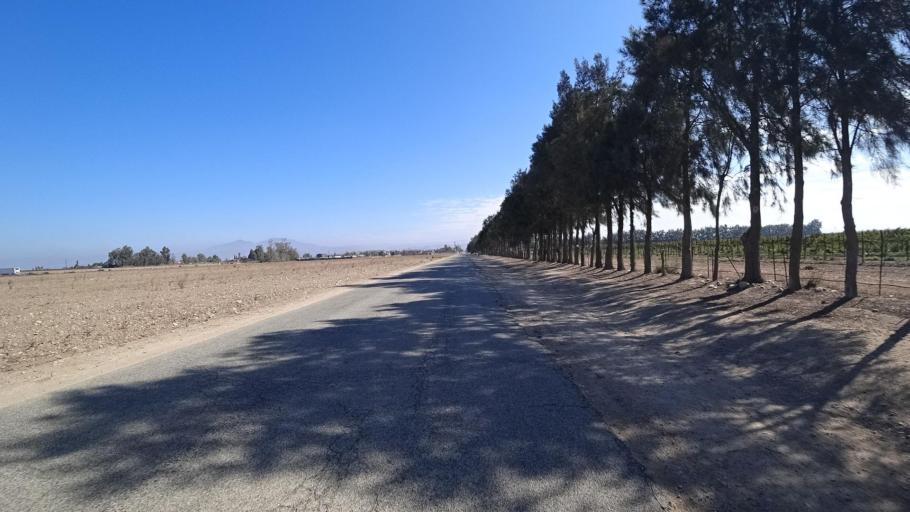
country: US
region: California
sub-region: Monterey County
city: Greenfield
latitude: 36.3105
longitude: -121.2630
